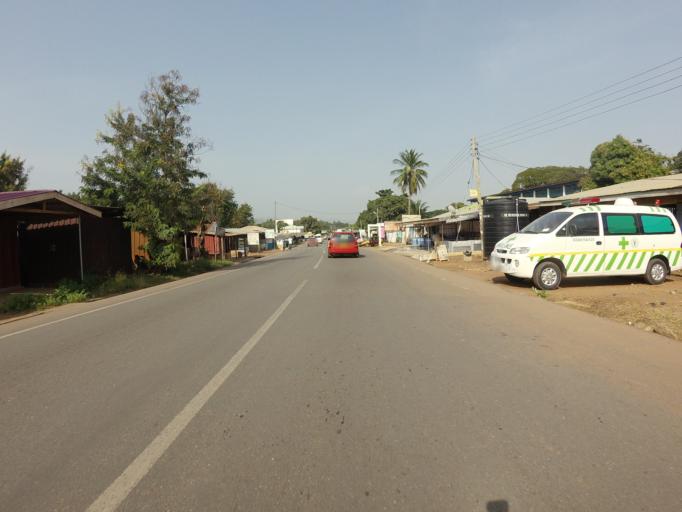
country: GH
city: Akropong
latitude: 6.1127
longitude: -0.0063
